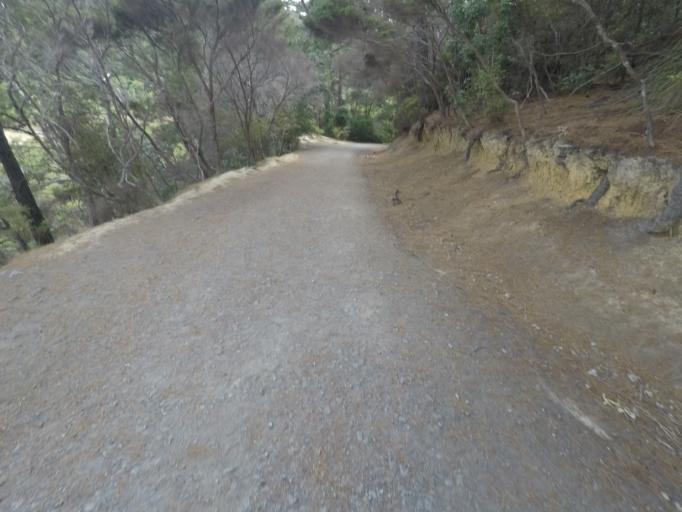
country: NZ
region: Auckland
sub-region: Auckland
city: North Shore
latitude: -36.8143
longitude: 174.6970
